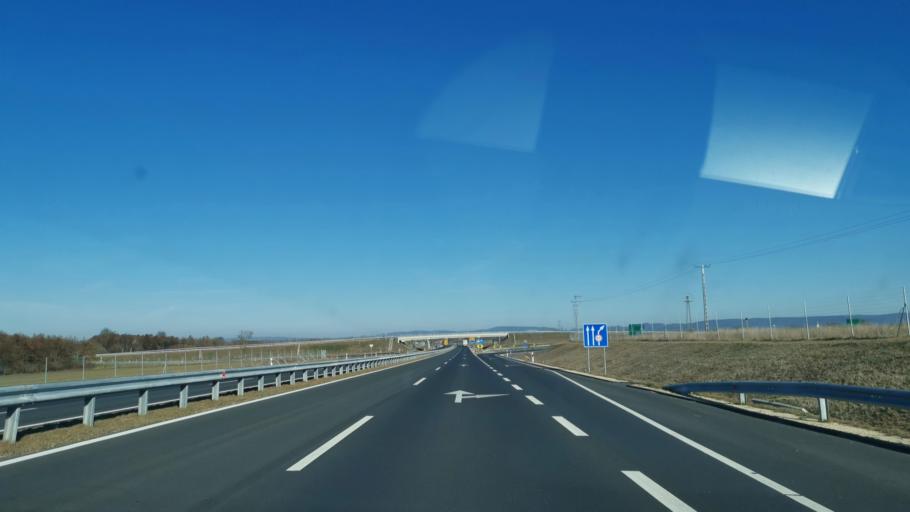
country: HU
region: Somogy
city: Balatonbereny
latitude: 46.6723
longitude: 17.2982
